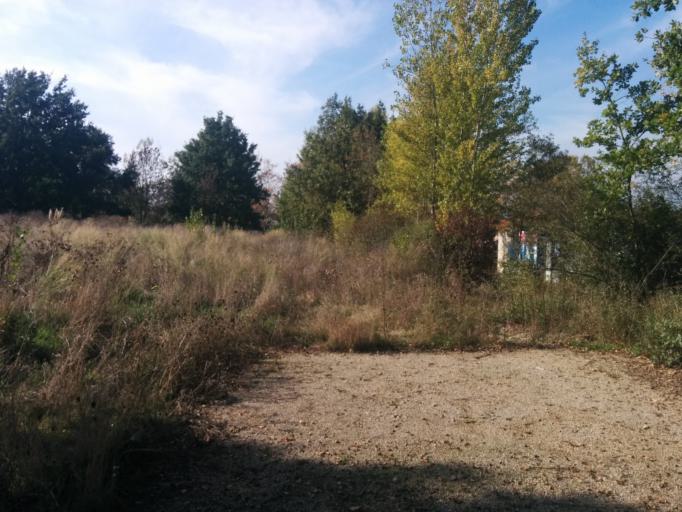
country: FR
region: Midi-Pyrenees
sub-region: Departement de la Haute-Garonne
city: Balma
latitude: 43.6293
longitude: 1.4954
